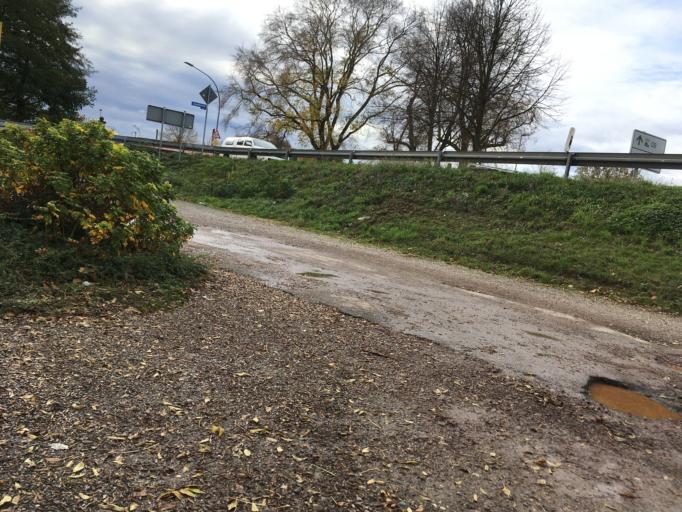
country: DE
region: Baden-Wuerttemberg
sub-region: Freiburg Region
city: Riegel
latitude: 48.1545
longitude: 7.7547
